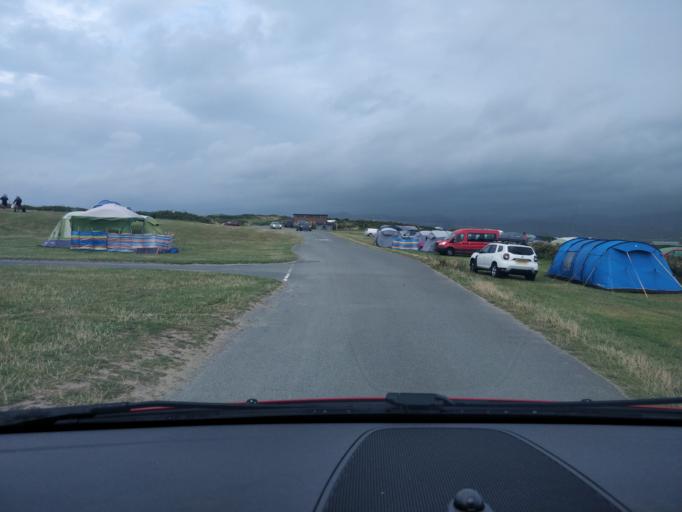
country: GB
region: Wales
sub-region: Gwynedd
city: Llanfair
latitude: 52.8150
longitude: -4.1495
